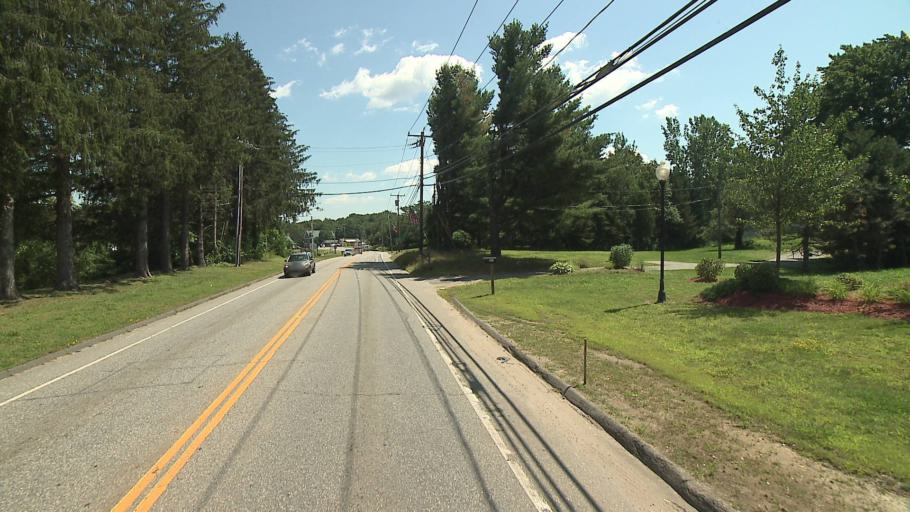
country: US
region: Connecticut
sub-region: Hartford County
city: Collinsville
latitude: 41.7701
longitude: -72.9700
